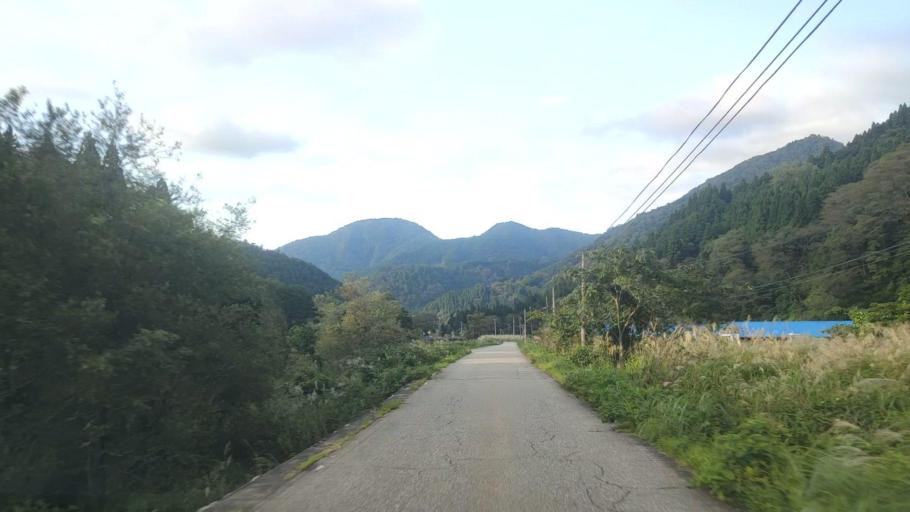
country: JP
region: Toyama
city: Yatsuomachi-higashikumisaka
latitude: 36.4674
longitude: 137.0860
